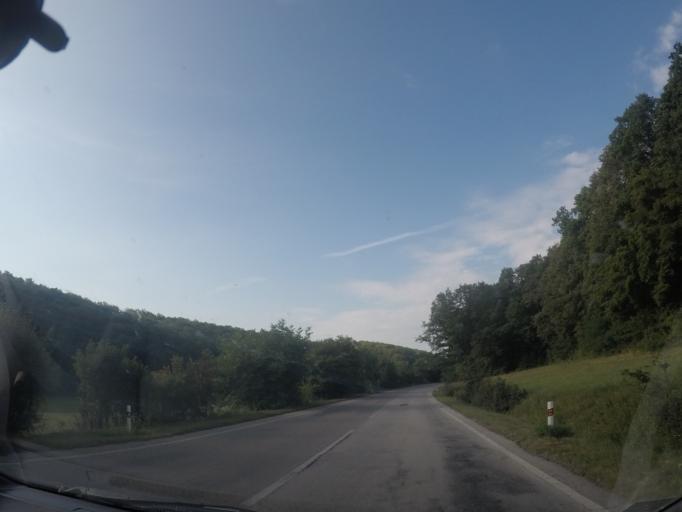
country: SK
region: Nitriansky
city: Zlate Moravce
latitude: 48.4481
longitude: 18.4130
